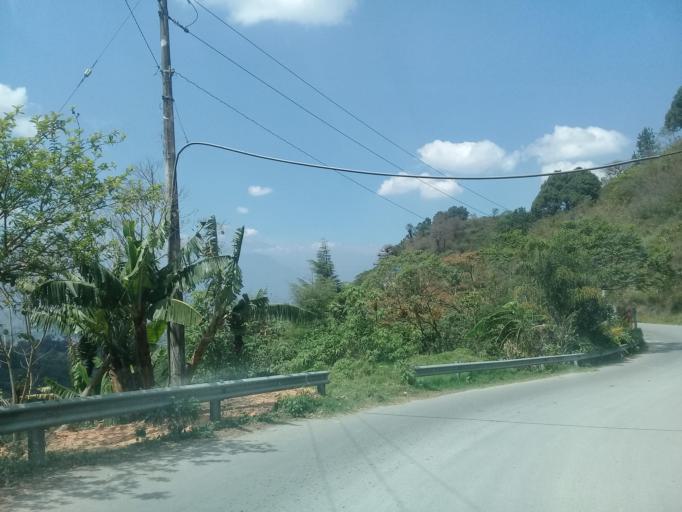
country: MX
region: Veracruz
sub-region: Tlilapan
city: Tonalixco
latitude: 18.7972
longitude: -97.0558
